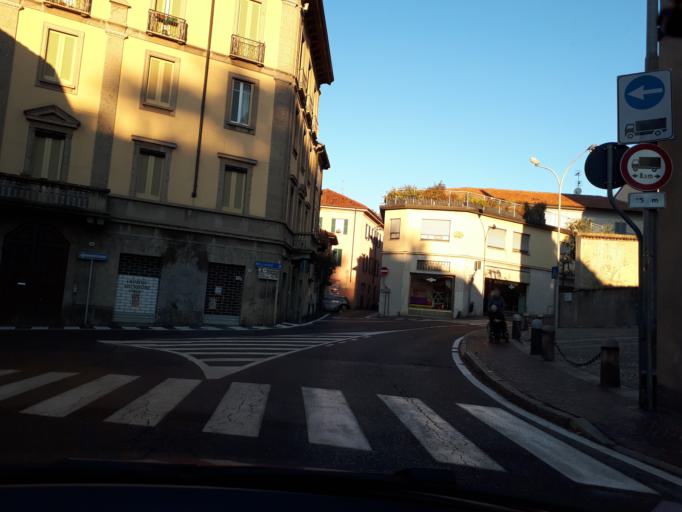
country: IT
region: Lombardy
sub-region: Provincia di Como
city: Brunate
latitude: 45.8154
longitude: 9.0847
